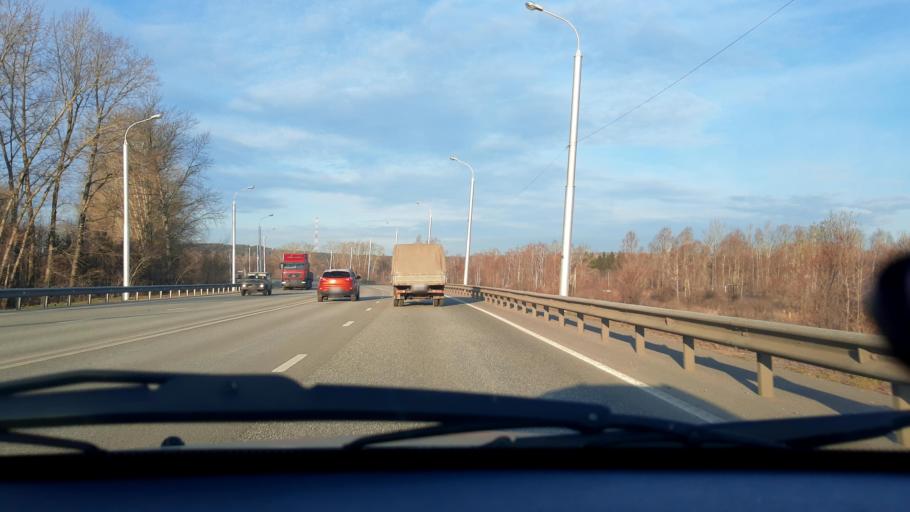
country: RU
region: Bashkortostan
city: Ufa
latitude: 54.8084
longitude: 56.1707
